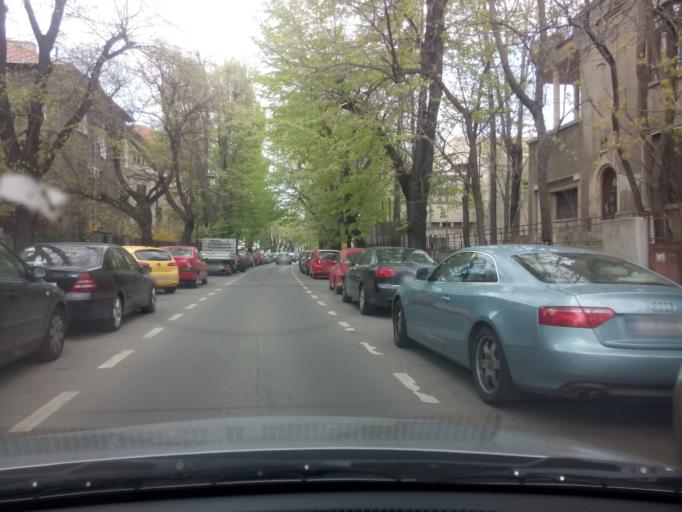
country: RO
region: Bucuresti
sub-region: Municipiul Bucuresti
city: Bucharest
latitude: 44.4559
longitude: 26.0941
